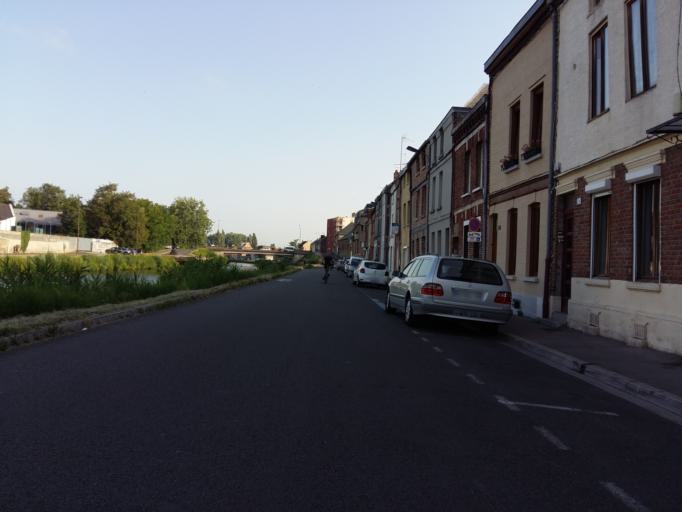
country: FR
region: Picardie
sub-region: Departement de la Somme
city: Amiens
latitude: 49.9017
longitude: 2.2879
